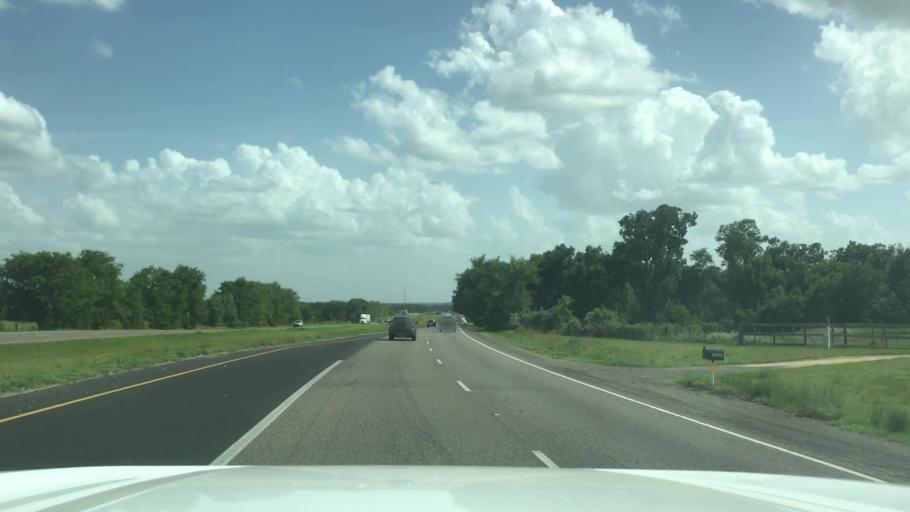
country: US
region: Texas
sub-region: Grimes County
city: Navasota
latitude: 30.3055
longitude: -96.0461
